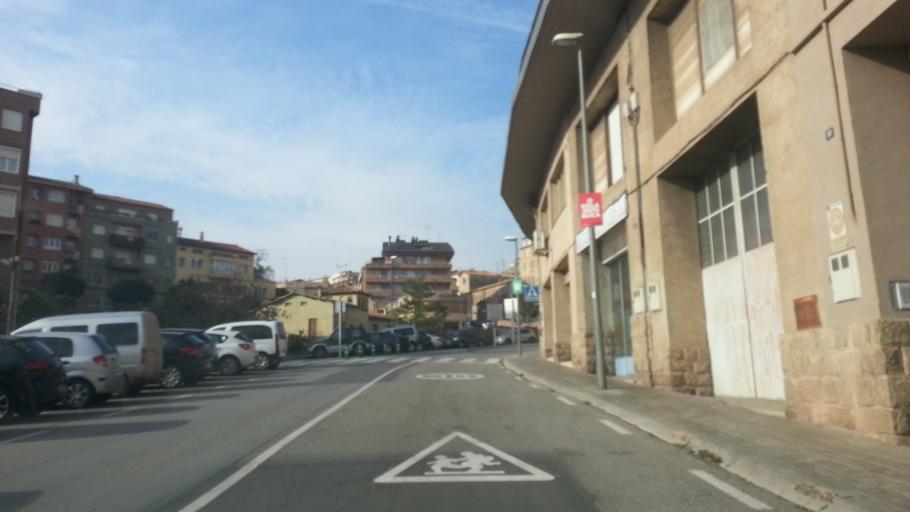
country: ES
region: Catalonia
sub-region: Provincia de Barcelona
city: Cardona
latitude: 41.9129
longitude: 1.6800
